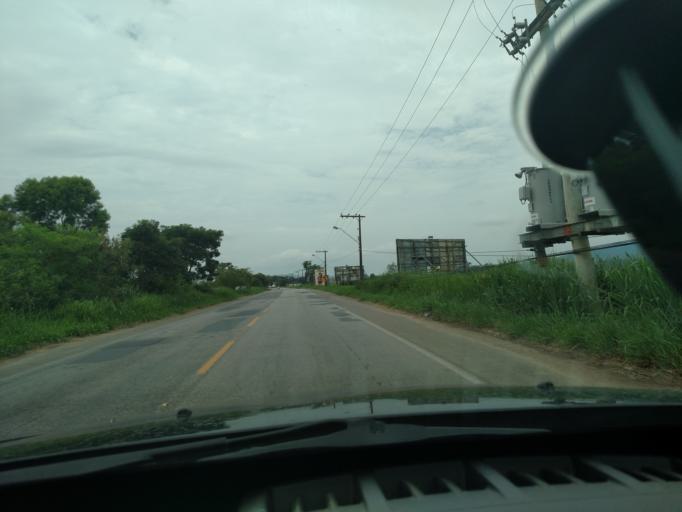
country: BR
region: Santa Catarina
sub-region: Itajai
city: Itajai
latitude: -26.8853
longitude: -48.8066
